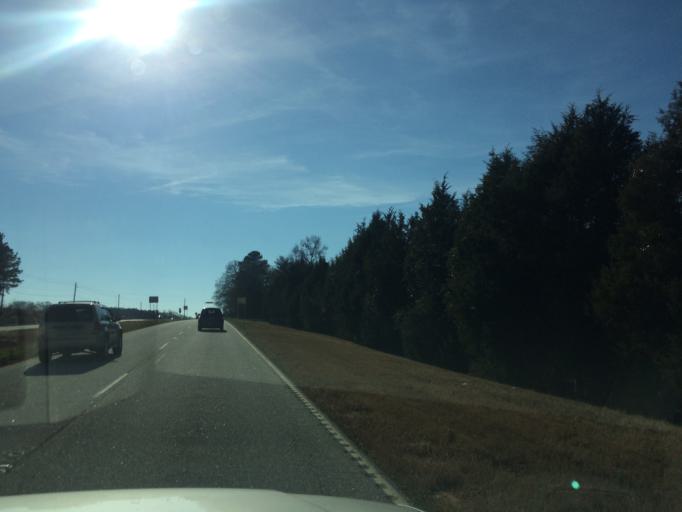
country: US
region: South Carolina
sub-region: Greenwood County
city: Greenwood
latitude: 34.2628
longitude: -82.0851
